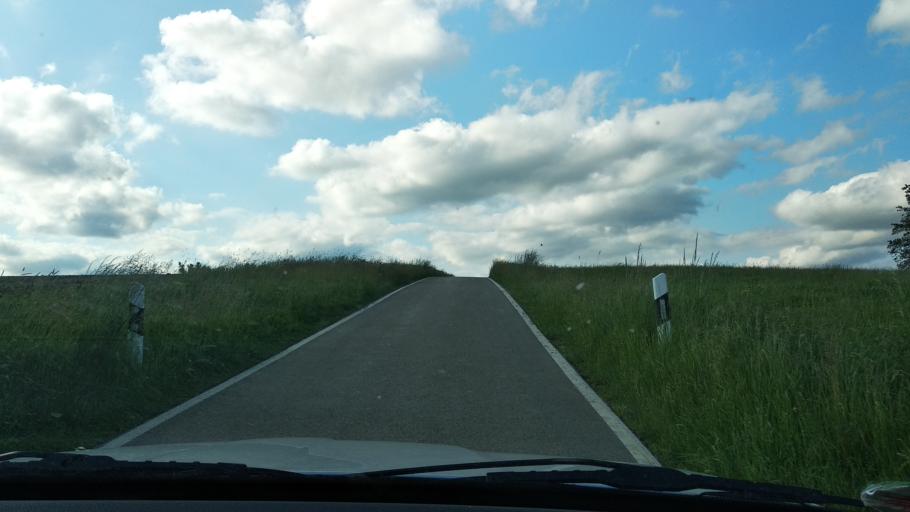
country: DE
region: Baden-Wuerttemberg
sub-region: Tuebingen Region
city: Aitrach
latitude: 47.9401
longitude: 10.0446
